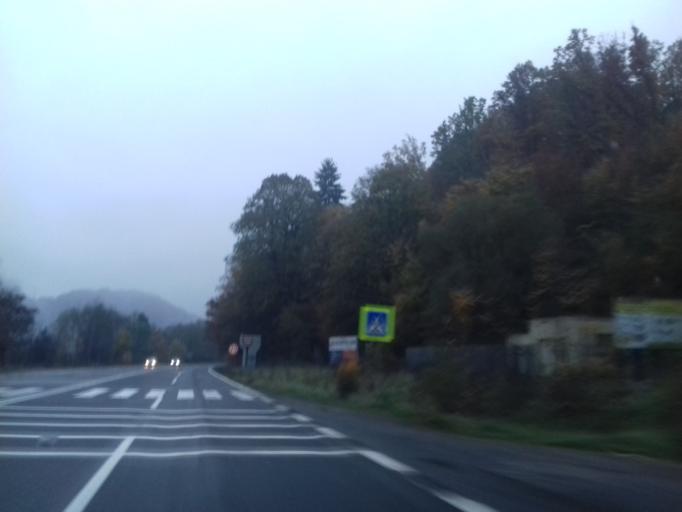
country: SK
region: Banskobystricky
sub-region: Okres Banska Bystrica
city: Banska Bystrica
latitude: 48.7881
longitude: 19.1074
